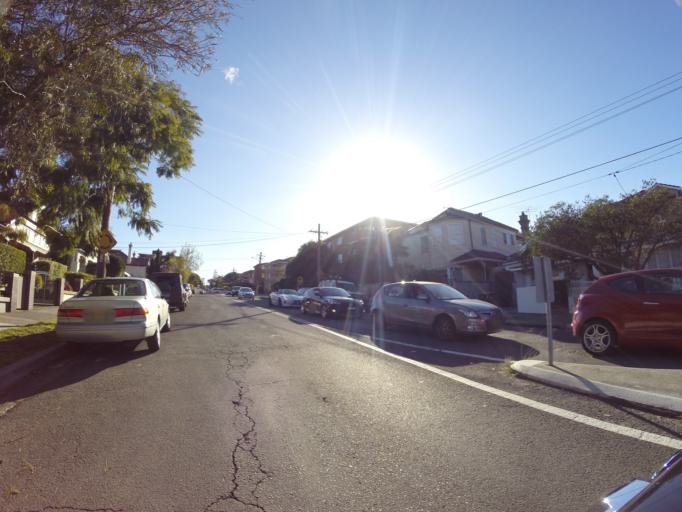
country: AU
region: New South Wales
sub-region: Waverley
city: Bondi
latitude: -33.8978
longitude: 151.2635
